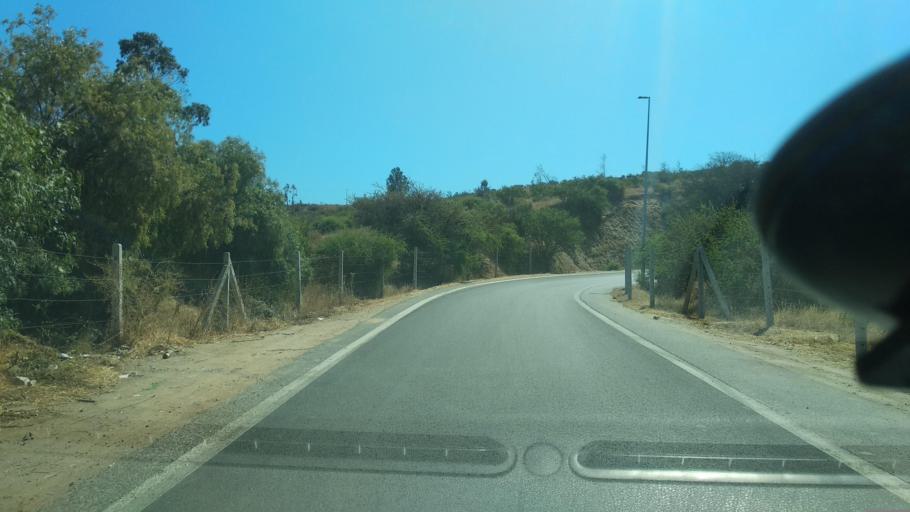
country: CL
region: Valparaiso
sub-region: Provincia de Marga Marga
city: Villa Alemana
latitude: -33.0692
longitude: -71.3738
